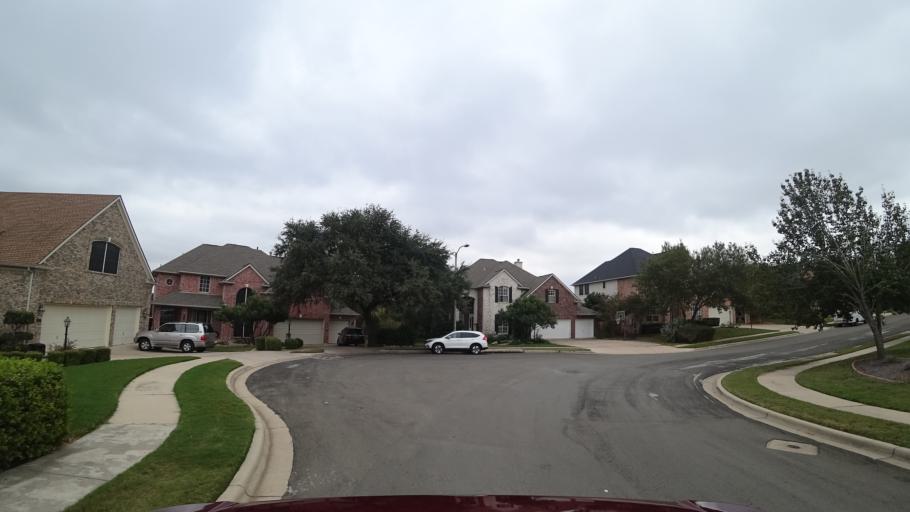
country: US
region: Texas
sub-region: Williamson County
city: Anderson Mill
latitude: 30.4316
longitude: -97.8310
